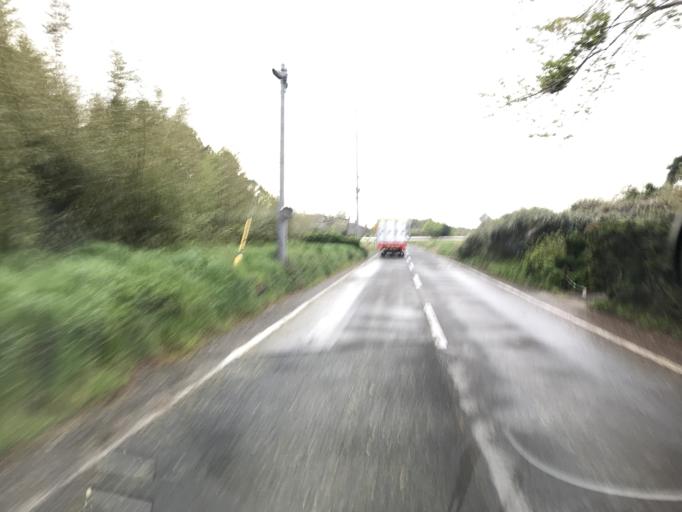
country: JP
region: Chiba
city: Yokaichiba
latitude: 35.7500
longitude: 140.5483
